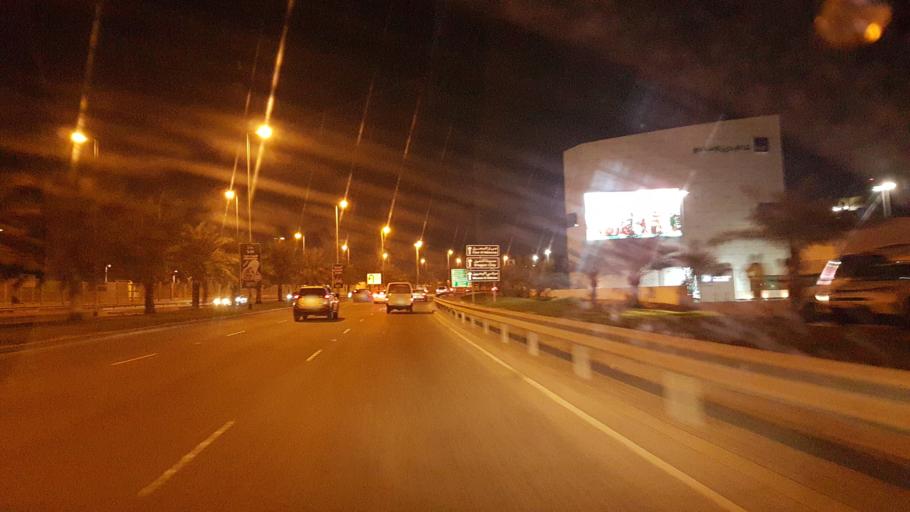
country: BH
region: Muharraq
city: Al Hadd
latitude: 26.2620
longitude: 50.6362
